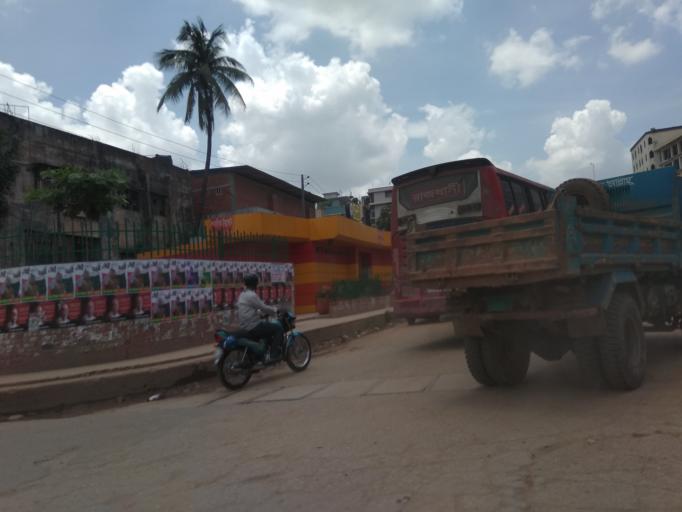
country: BD
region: Dhaka
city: Tungi
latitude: 23.8293
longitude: 90.3641
